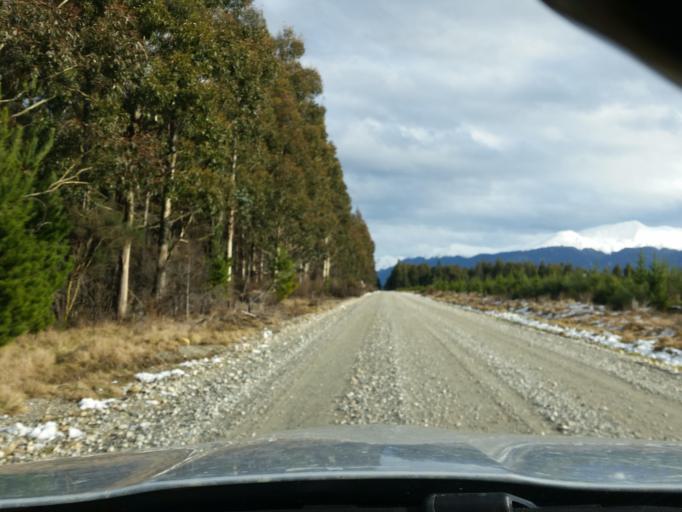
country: NZ
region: Southland
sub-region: Southland District
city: Te Anau
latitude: -45.7851
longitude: 167.5718
